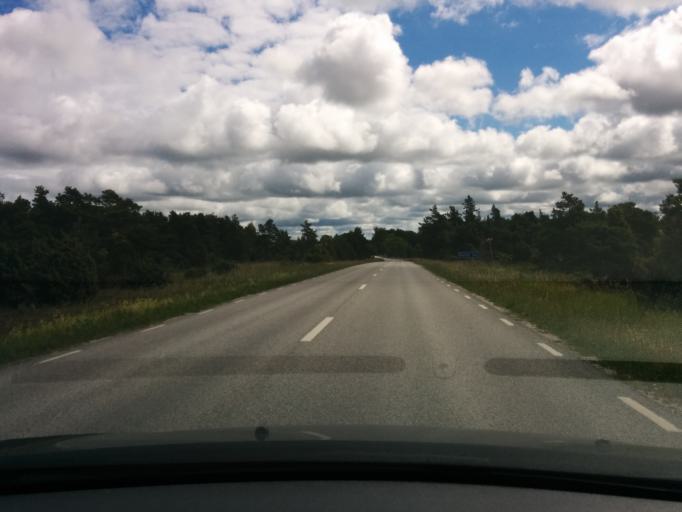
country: SE
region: Gotland
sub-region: Gotland
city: Visby
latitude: 57.6380
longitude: 18.4696
